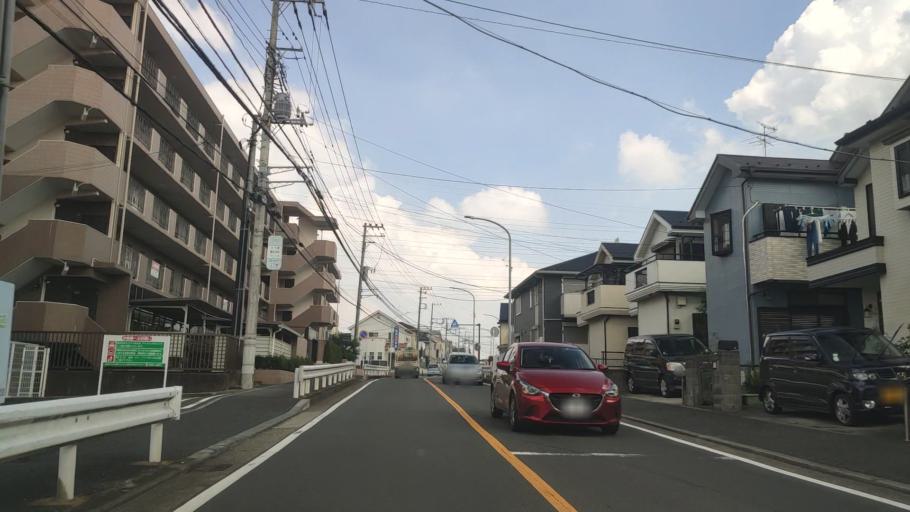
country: JP
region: Kanagawa
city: Minami-rinkan
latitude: 35.4507
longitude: 139.5030
